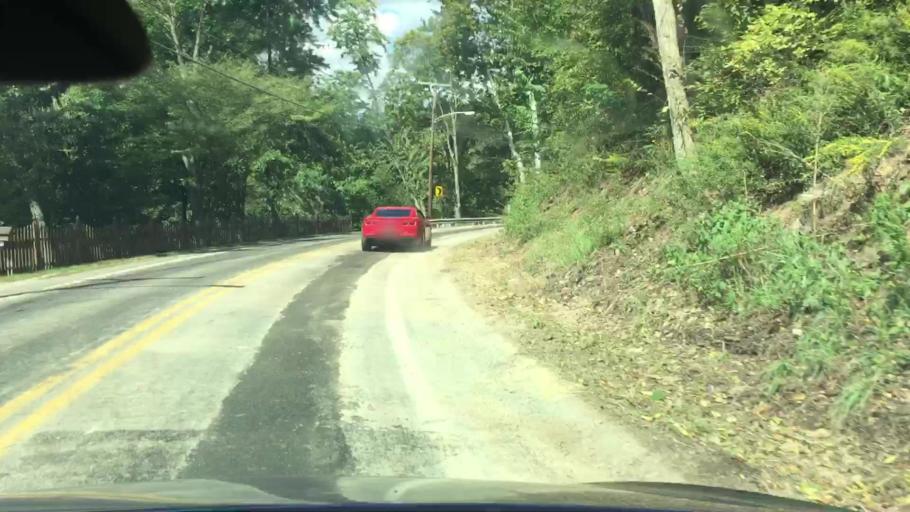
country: US
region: Pennsylvania
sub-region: Allegheny County
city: Russellton
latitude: 40.5854
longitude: -79.8278
